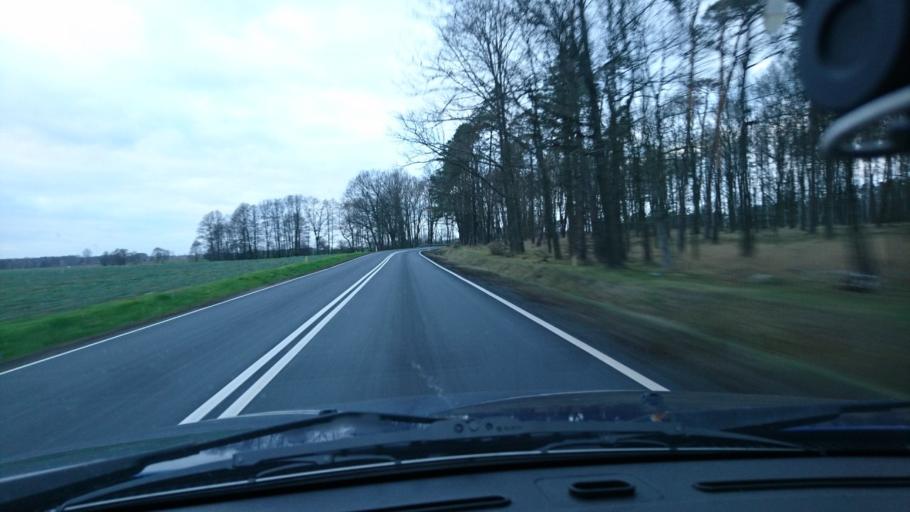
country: PL
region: Opole Voivodeship
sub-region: Powiat kluczborski
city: Byczyna
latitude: 51.1479
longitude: 18.1873
